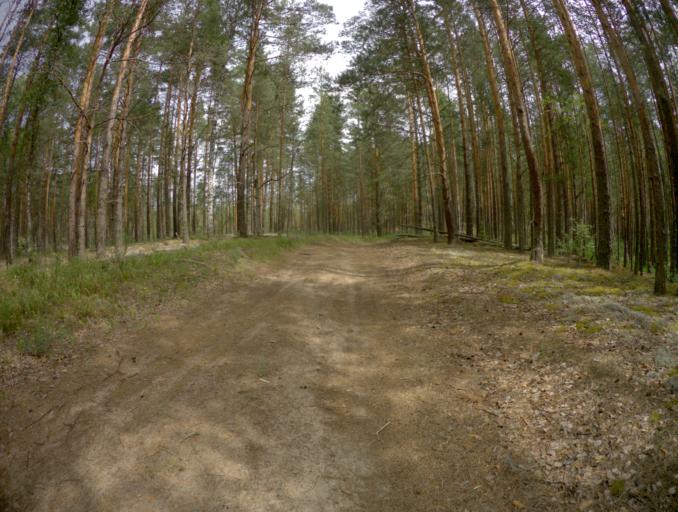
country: RU
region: Nizjnij Novgorod
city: Frolishchi
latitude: 56.3152
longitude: 42.6698
